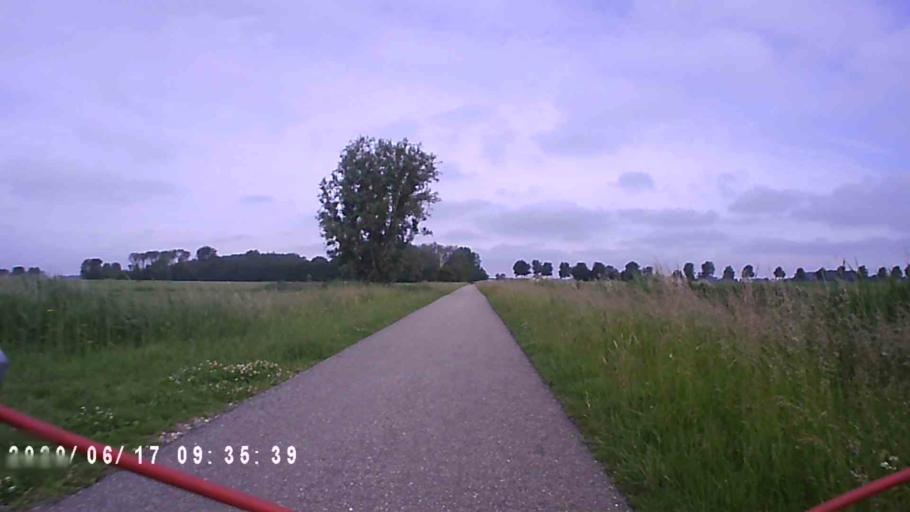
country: NL
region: Groningen
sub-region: Gemeente De Marne
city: Ulrum
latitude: 53.3497
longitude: 6.3761
